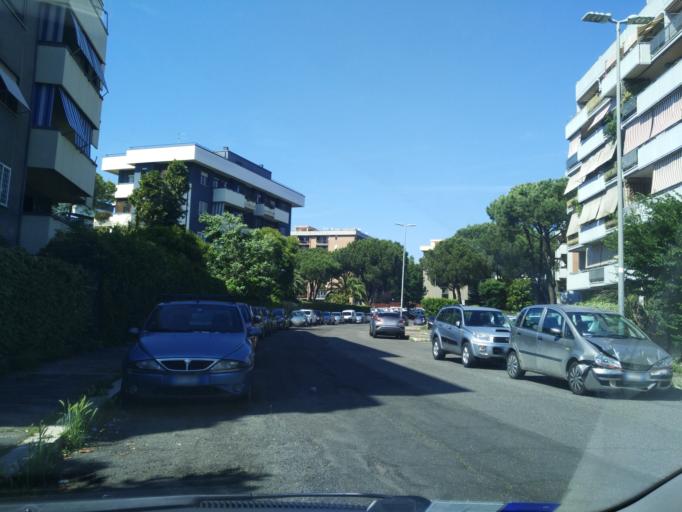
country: IT
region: Latium
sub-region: Citta metropolitana di Roma Capitale
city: Vitinia
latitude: 41.8086
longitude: 12.4349
